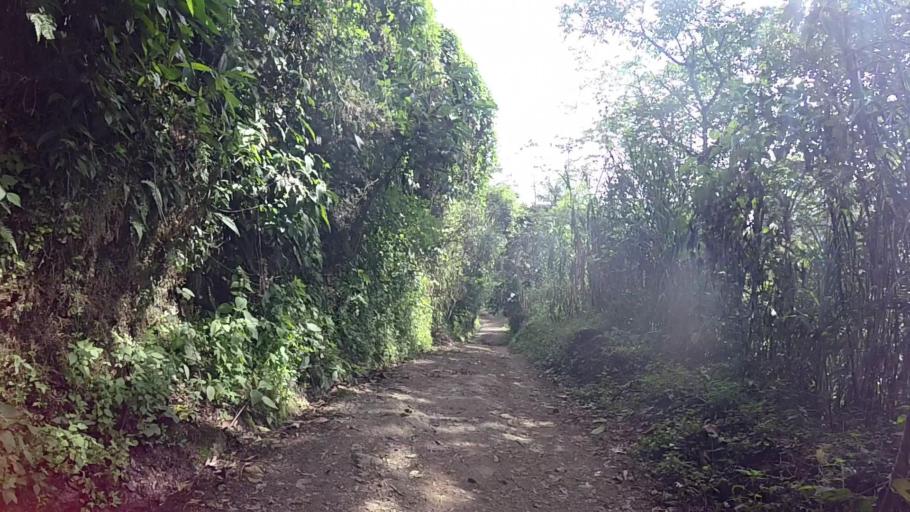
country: CO
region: Quindio
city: Salento
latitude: 4.6466
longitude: -75.5816
